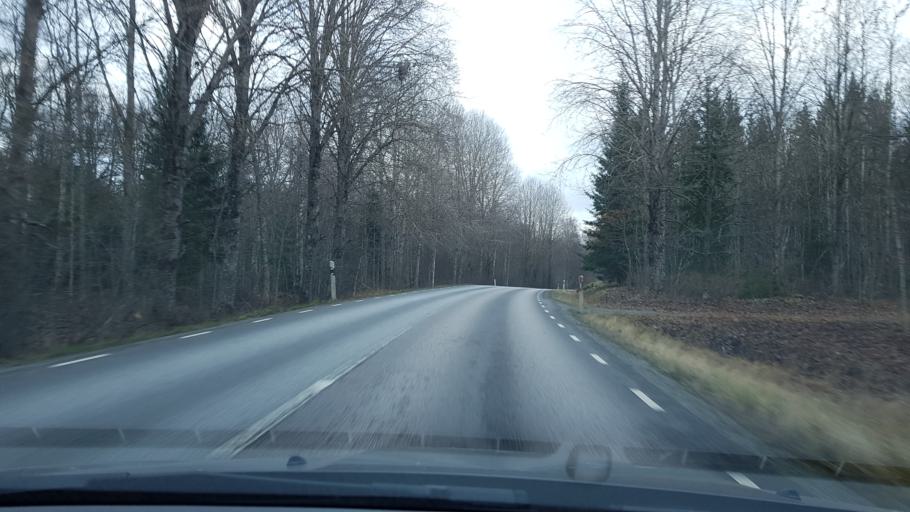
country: SE
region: Stockholm
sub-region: Norrtalje Kommun
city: Skanninge
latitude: 60.0297
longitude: 18.4228
